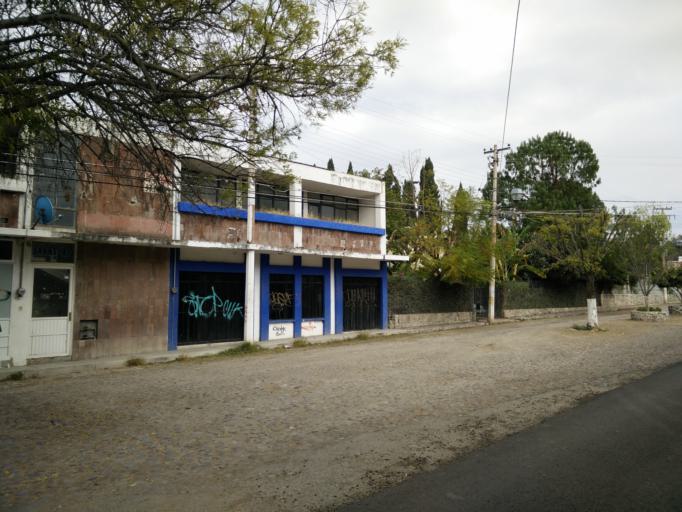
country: MX
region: Queretaro
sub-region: Tequisquiapan
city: Tequisquiapan
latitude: 20.5182
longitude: -99.8833
